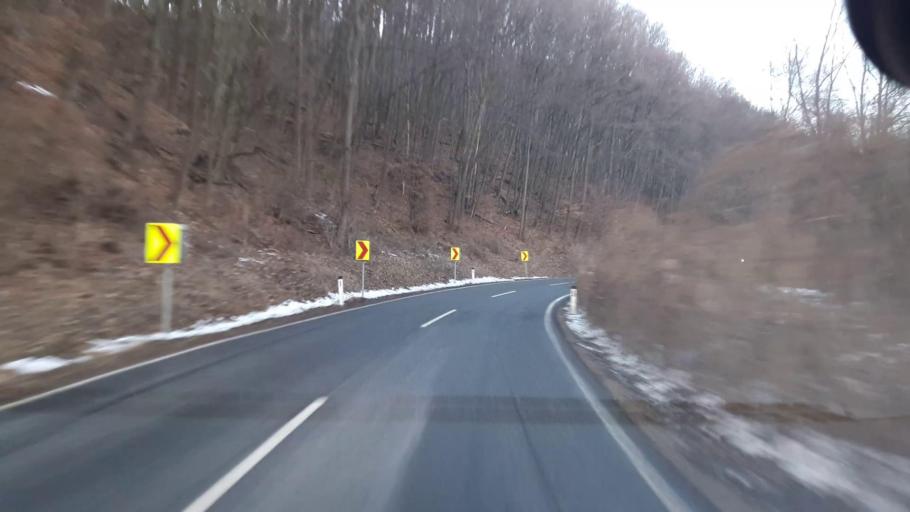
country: AT
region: Lower Austria
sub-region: Politischer Bezirk Wien-Umgebung
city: Klosterneuburg
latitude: 48.2739
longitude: 16.2750
